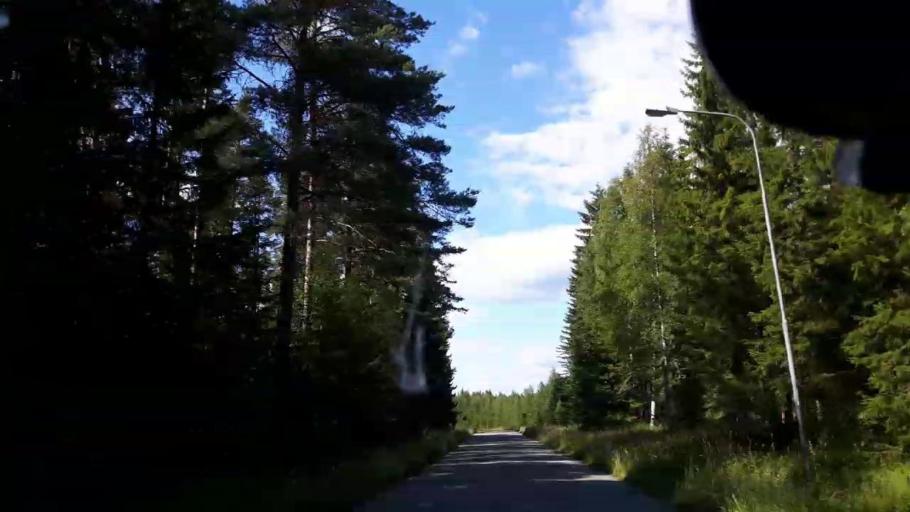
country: SE
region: Jaemtland
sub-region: Braecke Kommun
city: Braecke
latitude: 62.8338
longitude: 15.3086
